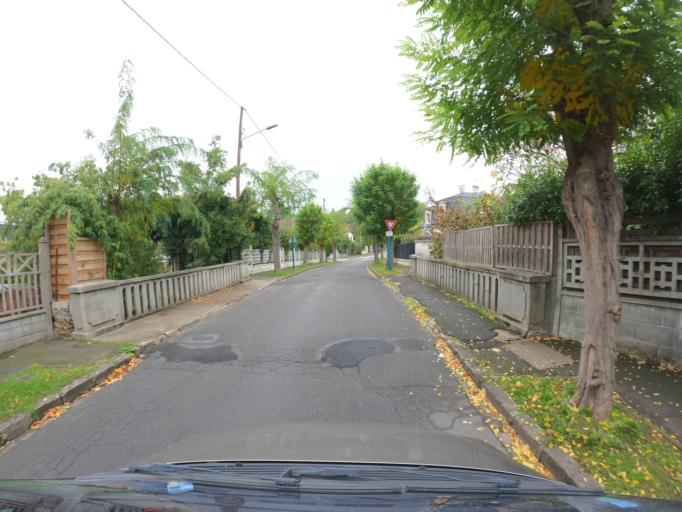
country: FR
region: Ile-de-France
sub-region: Departement du Val-de-Marne
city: Sucy-en-Brie
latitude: 48.7784
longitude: 2.5146
